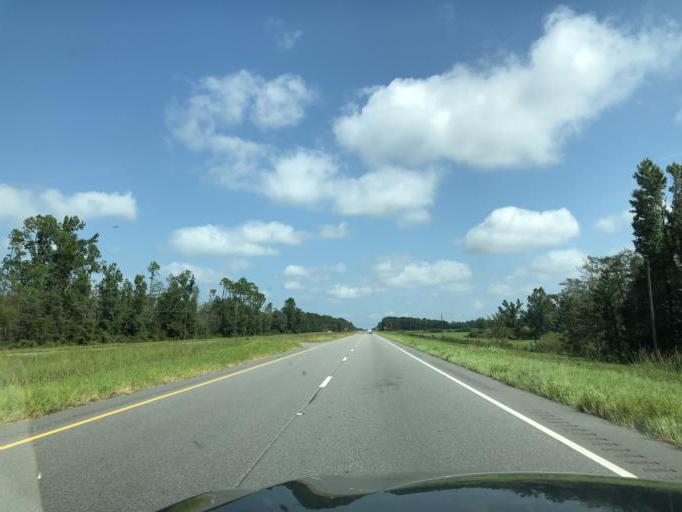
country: US
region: Alabama
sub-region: Houston County
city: Cottonwood
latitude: 31.0296
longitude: -85.4068
